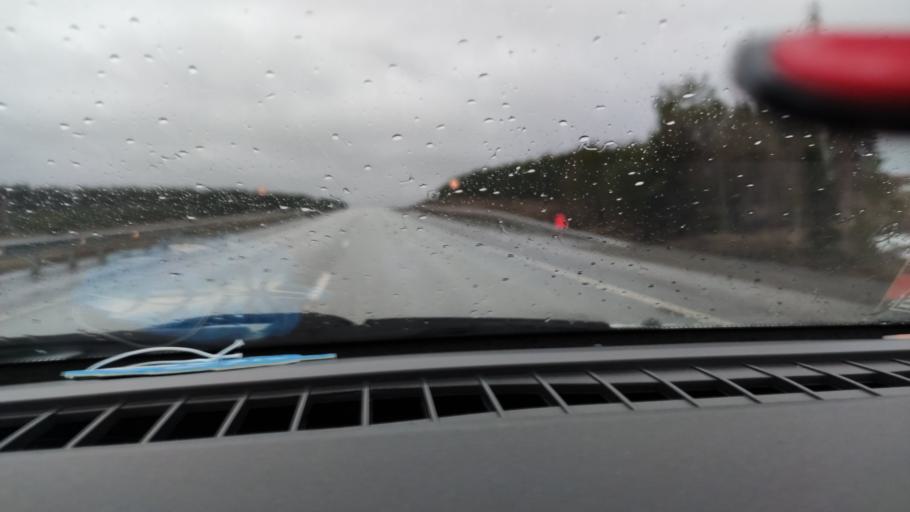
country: RU
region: Udmurtiya
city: Alnashi
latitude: 56.0549
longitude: 52.3926
